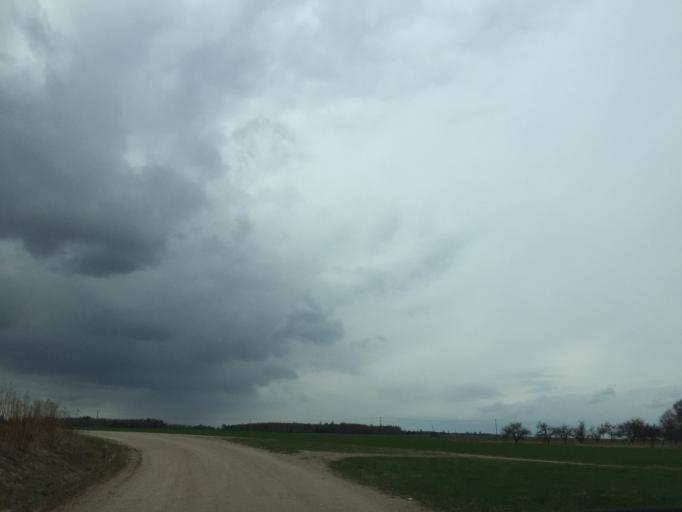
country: LV
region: Priekuli
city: Priekuli
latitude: 57.3379
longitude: 25.3700
